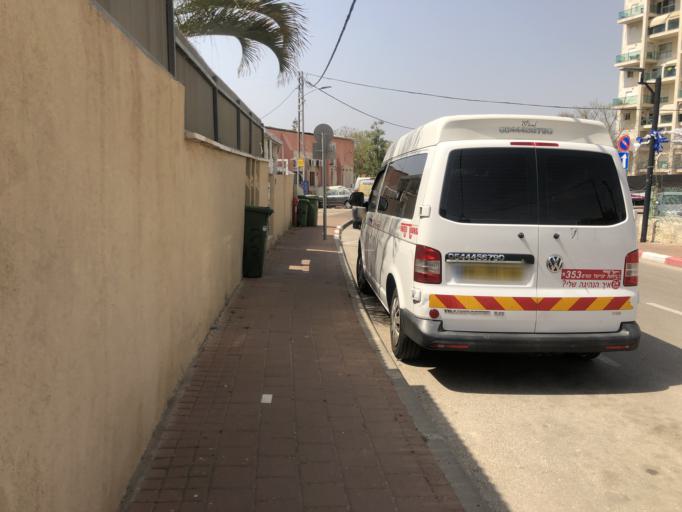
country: IL
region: Central District
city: Rosh Ha'Ayin
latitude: 32.0958
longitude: 34.9390
